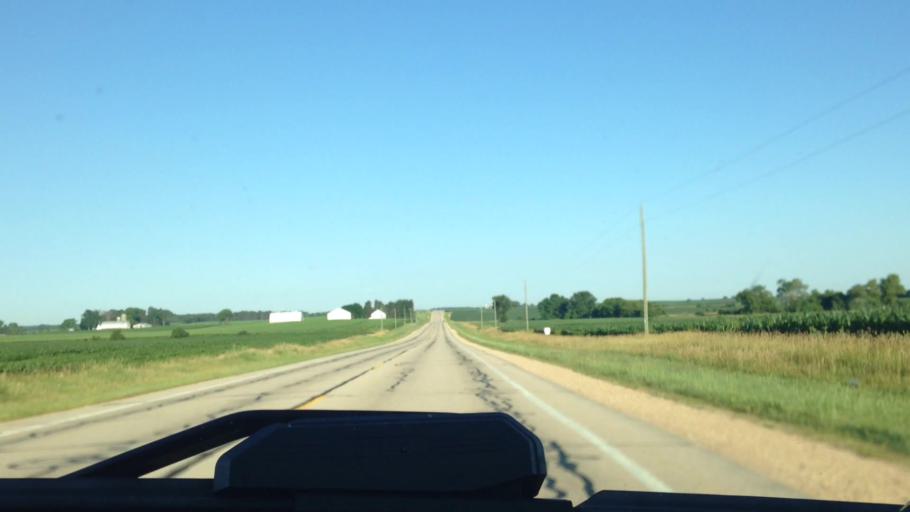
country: US
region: Wisconsin
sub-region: Columbia County
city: Rio
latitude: 43.3411
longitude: -89.2036
